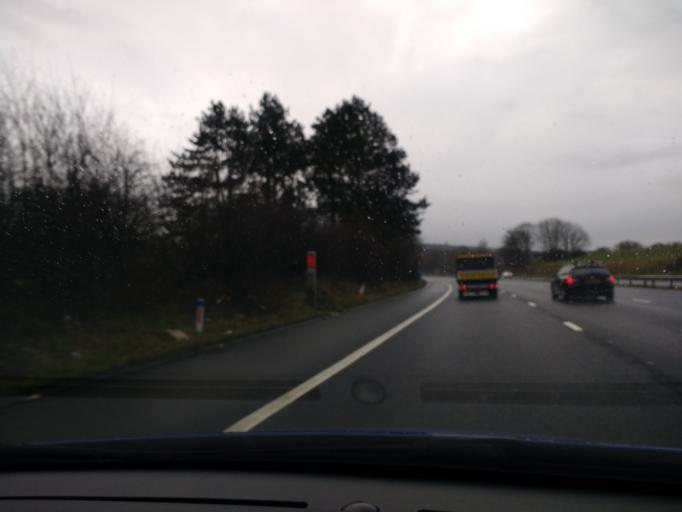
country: GB
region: England
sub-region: Lancashire
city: Bolton le Sands
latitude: 54.0789
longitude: -2.7713
